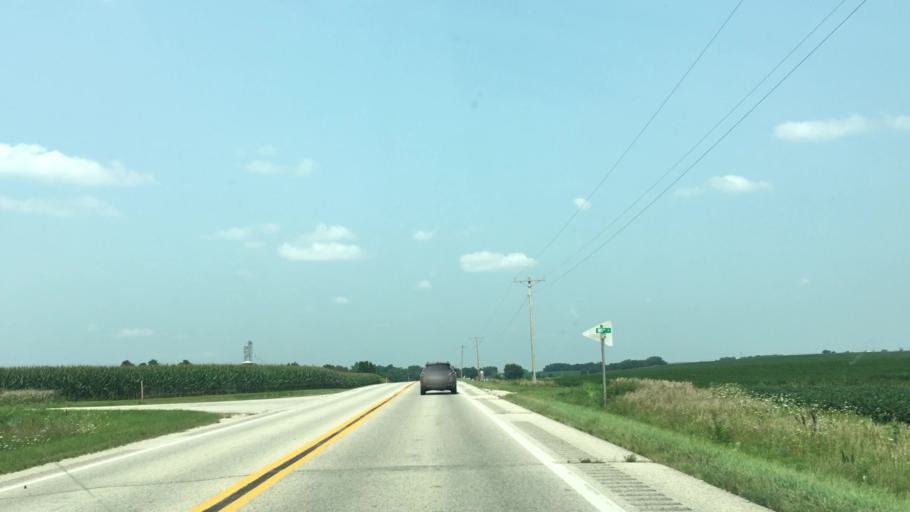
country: US
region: Iowa
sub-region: Buchanan County
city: Independence
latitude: 42.5193
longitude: -91.8898
